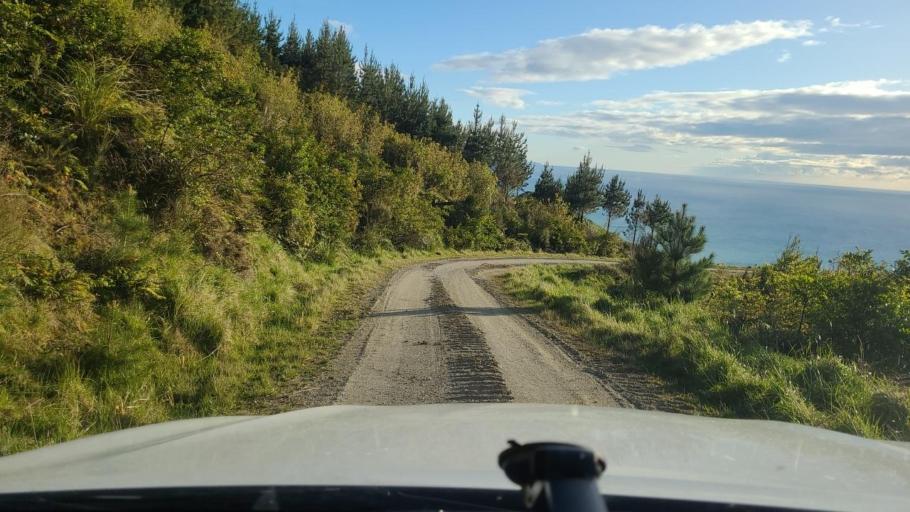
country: NZ
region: Gisborne
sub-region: Gisborne District
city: Gisborne
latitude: -38.9464
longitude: 177.8881
